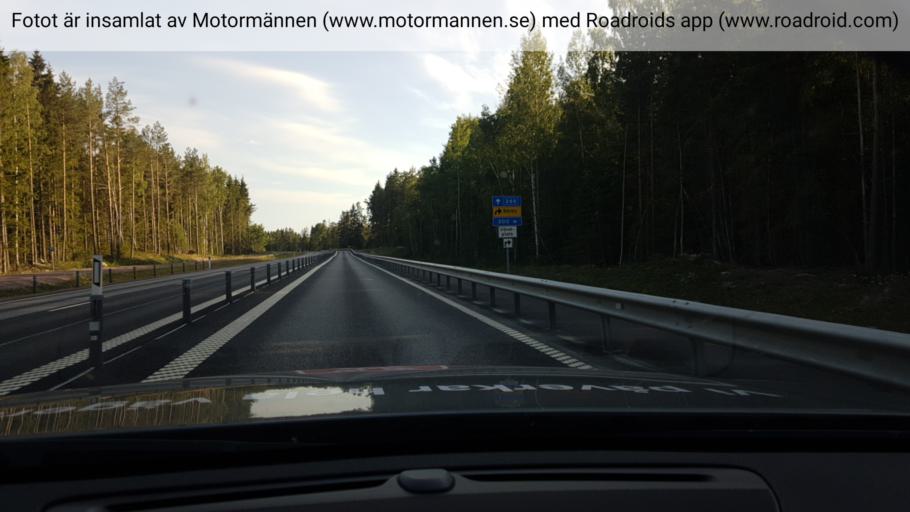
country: SE
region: Uppsala
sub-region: Osthammars Kommun
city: Gimo
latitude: 60.1104
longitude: 18.1282
